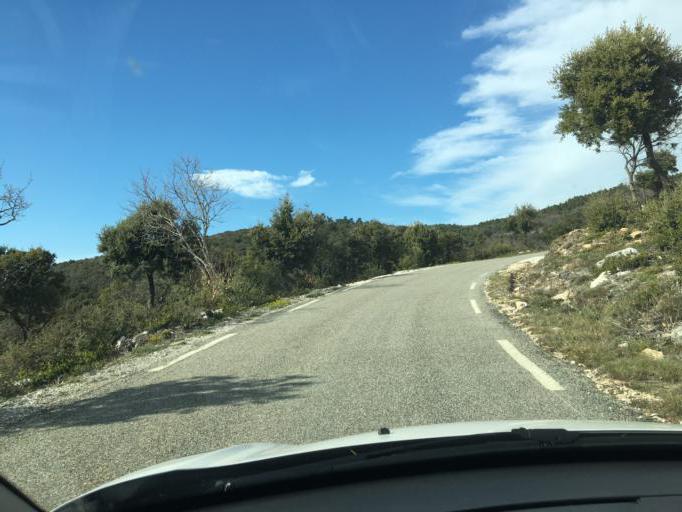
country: FR
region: Provence-Alpes-Cote d'Azur
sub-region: Departement du Vaucluse
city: Saint-Saturnin-les-Apt
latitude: 43.9601
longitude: 5.4600
